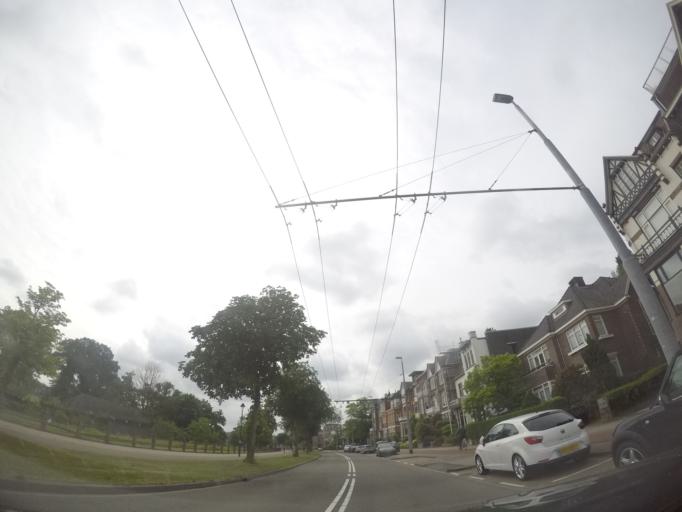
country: NL
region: Gelderland
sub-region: Gemeente Arnhem
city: Burgemeesterswijk
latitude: 51.9879
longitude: 5.9009
